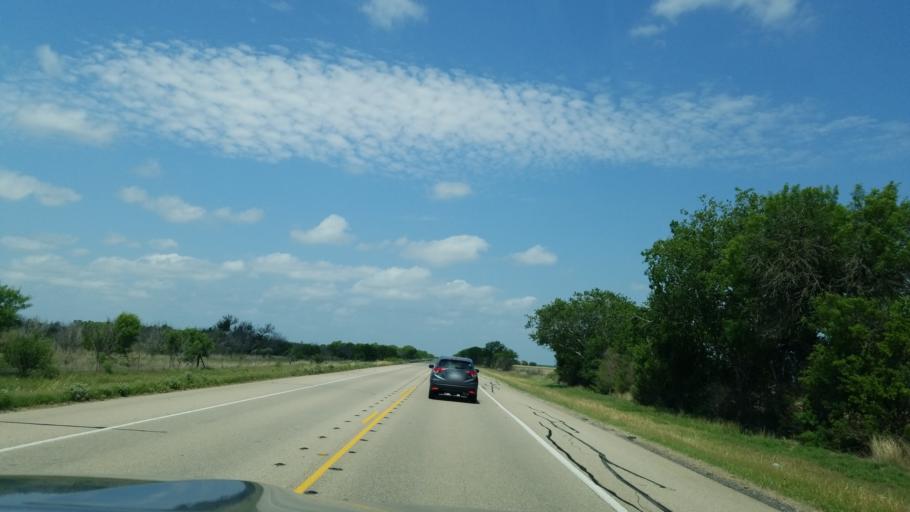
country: US
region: Texas
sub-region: Frio County
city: Pearsall
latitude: 29.0066
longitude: -99.1531
